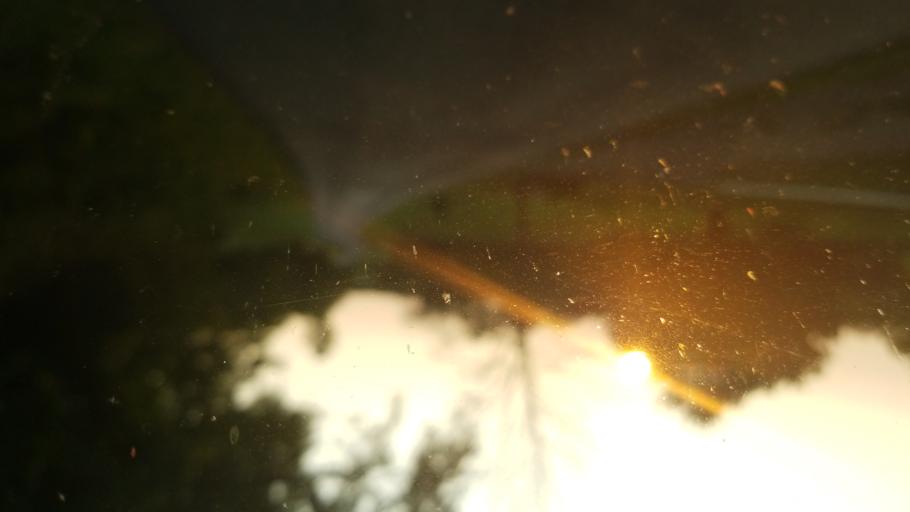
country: US
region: Ohio
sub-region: Knox County
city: Danville
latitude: 40.5375
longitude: -82.3207
